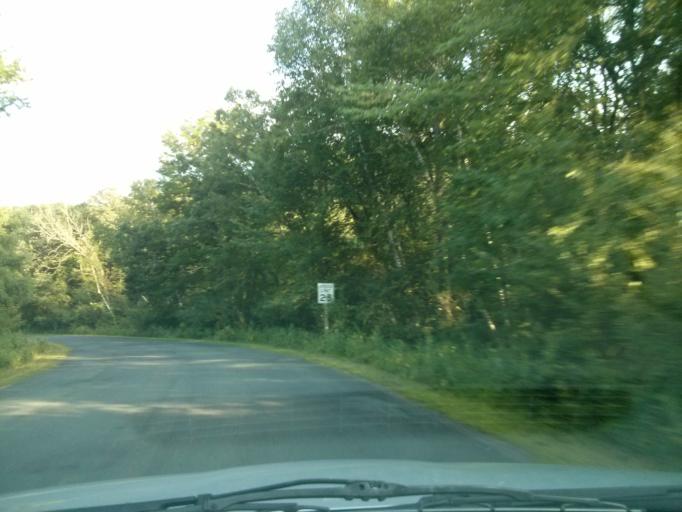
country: US
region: Wisconsin
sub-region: Saint Croix County
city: North Hudson
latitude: 45.0112
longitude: -92.7060
